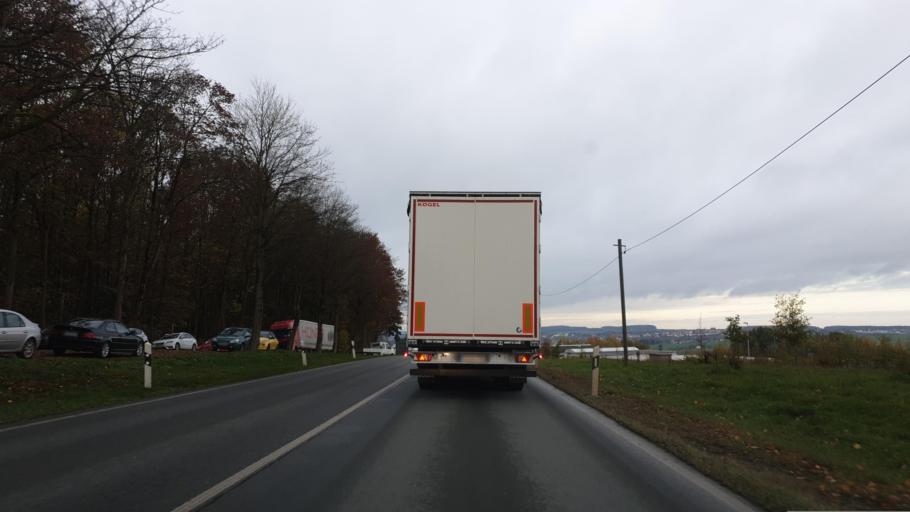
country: DE
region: Saxony
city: Reichenbach/Vogtland
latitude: 50.5964
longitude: 12.3329
